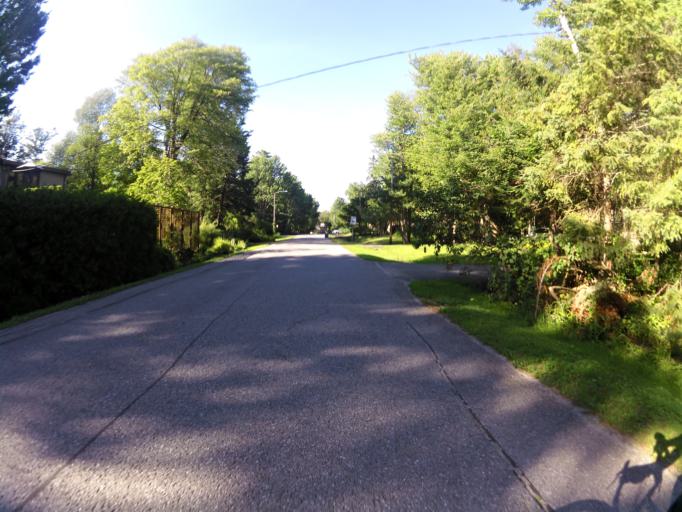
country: CA
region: Ontario
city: Ottawa
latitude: 45.3164
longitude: -75.7263
